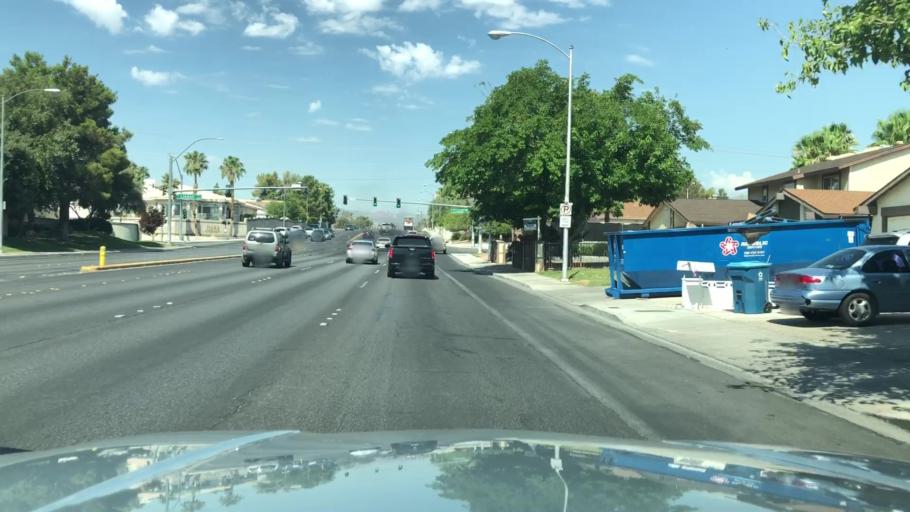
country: US
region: Nevada
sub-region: Clark County
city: Spring Valley
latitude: 36.1297
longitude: -115.2154
